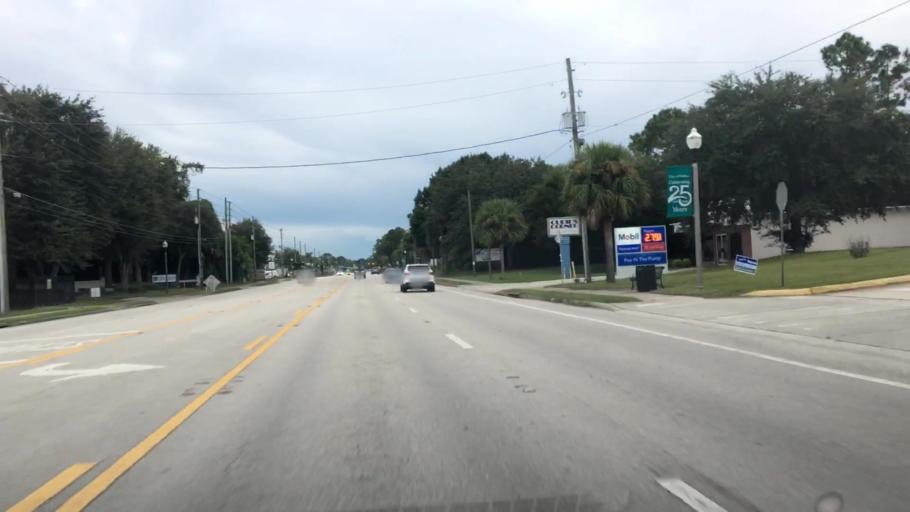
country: US
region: Florida
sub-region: Volusia County
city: DeBary
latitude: 28.8893
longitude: -81.3072
